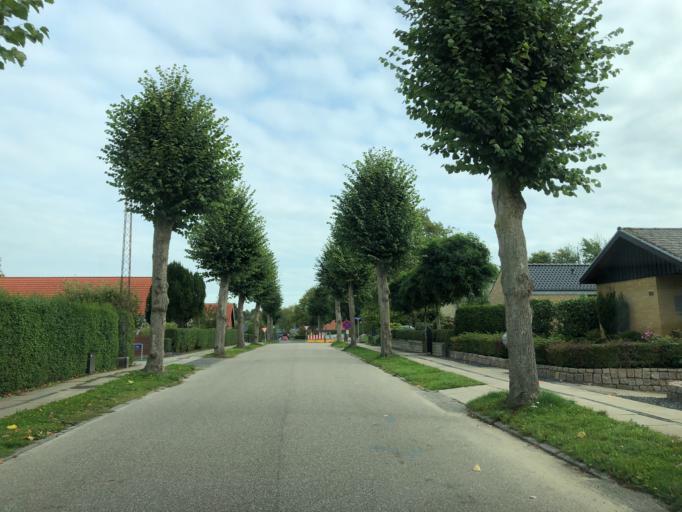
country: DK
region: South Denmark
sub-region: Sonderborg Kommune
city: Sonderborg
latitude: 54.9062
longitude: 9.8154
